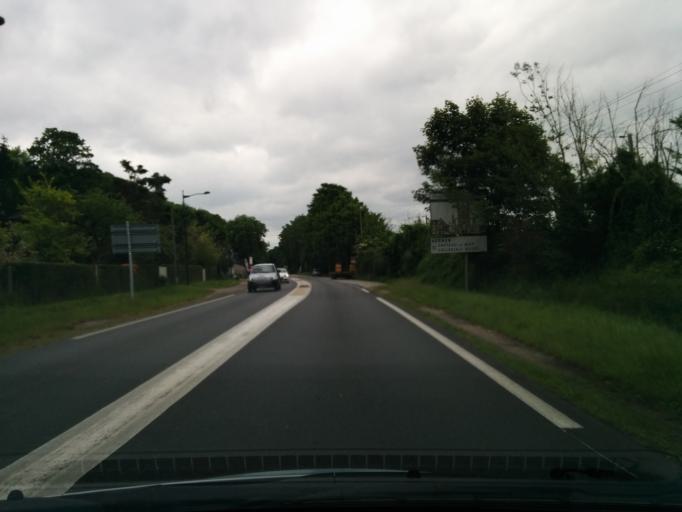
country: FR
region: Ile-de-France
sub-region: Departement des Yvelines
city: Limetz-Villez
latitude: 49.0755
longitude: 1.5109
